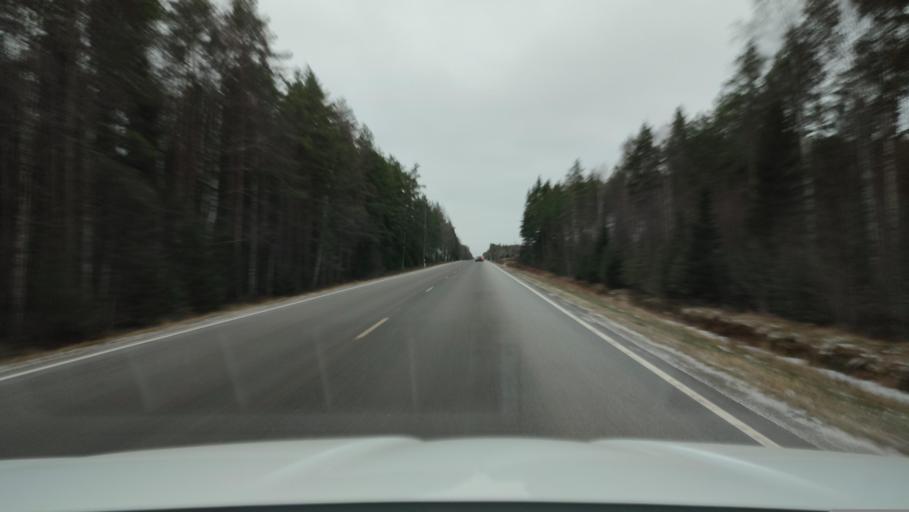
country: FI
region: Ostrobothnia
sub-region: Sydosterbotten
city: Naerpes
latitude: 62.5703
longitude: 21.4865
